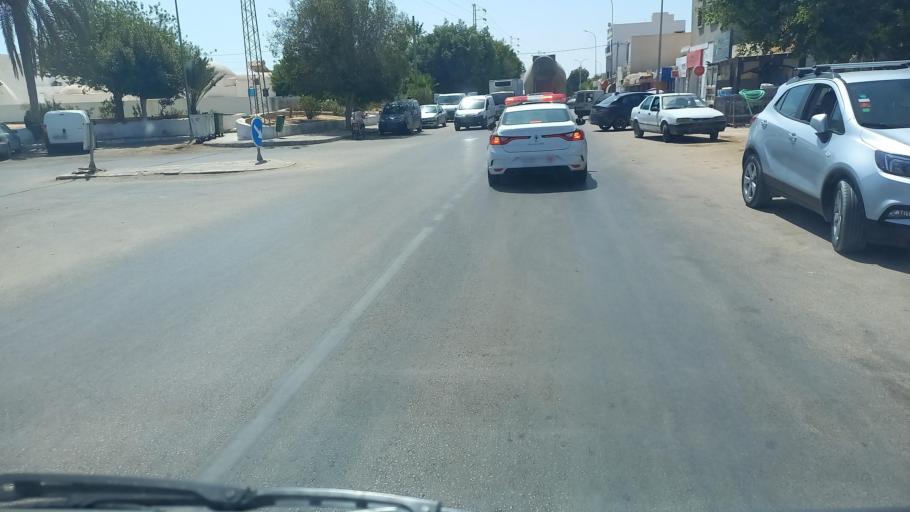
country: TN
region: Madanin
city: Houmt Souk
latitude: 33.8026
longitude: 10.8830
